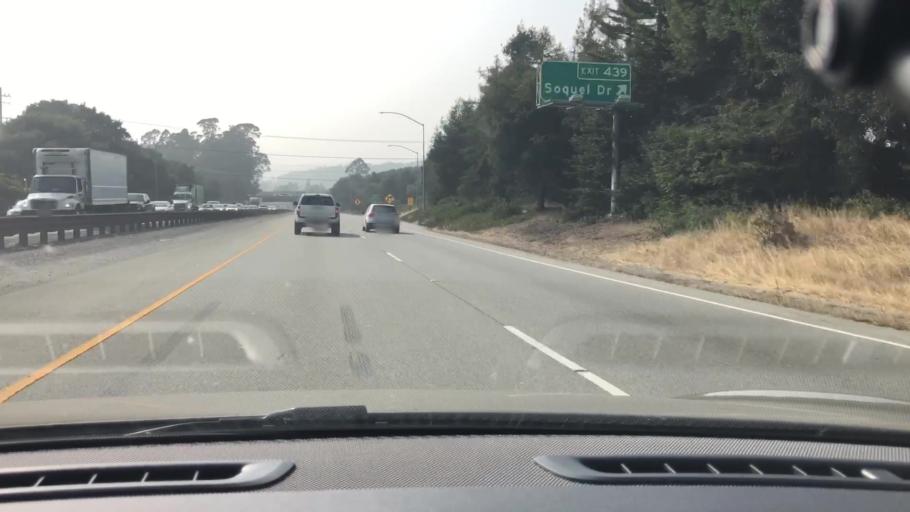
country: US
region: California
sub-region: Santa Cruz County
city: Live Oak
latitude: 36.9864
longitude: -121.9825
